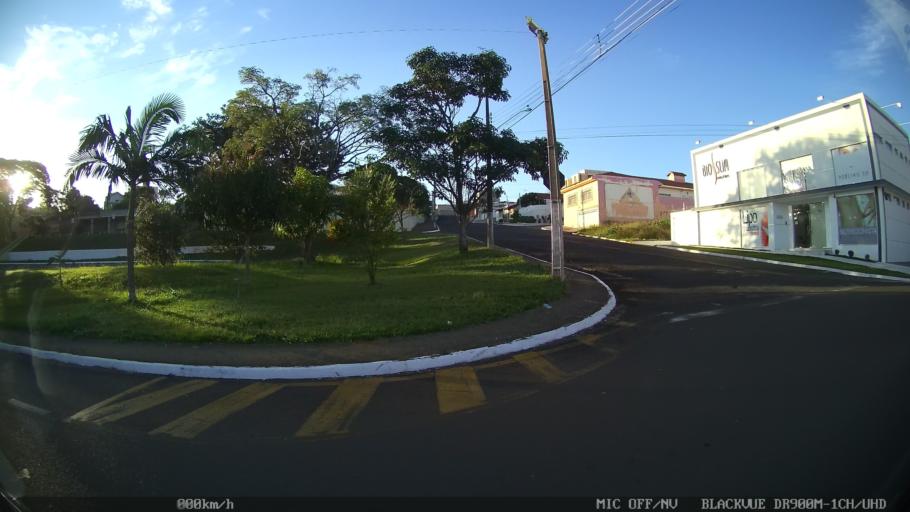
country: BR
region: Sao Paulo
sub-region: Franca
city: Franca
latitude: -20.5307
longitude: -47.3867
